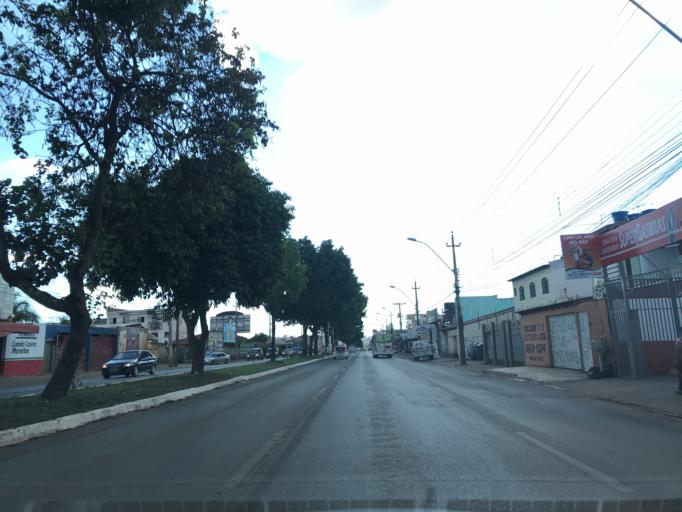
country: BR
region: Federal District
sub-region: Brasilia
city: Brasilia
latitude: -15.8003
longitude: -48.0591
